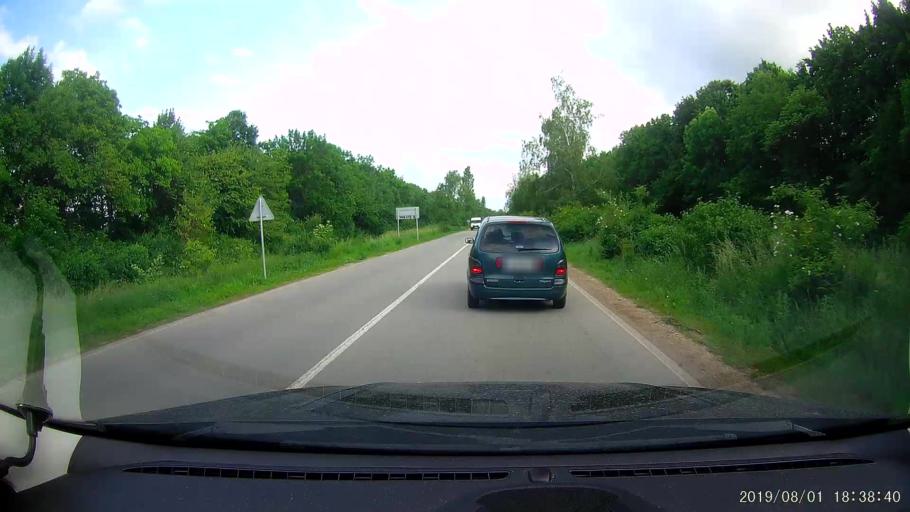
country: BG
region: Shumen
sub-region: Obshtina Khitrino
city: Gara Khitrino
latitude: 43.3990
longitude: 26.9161
